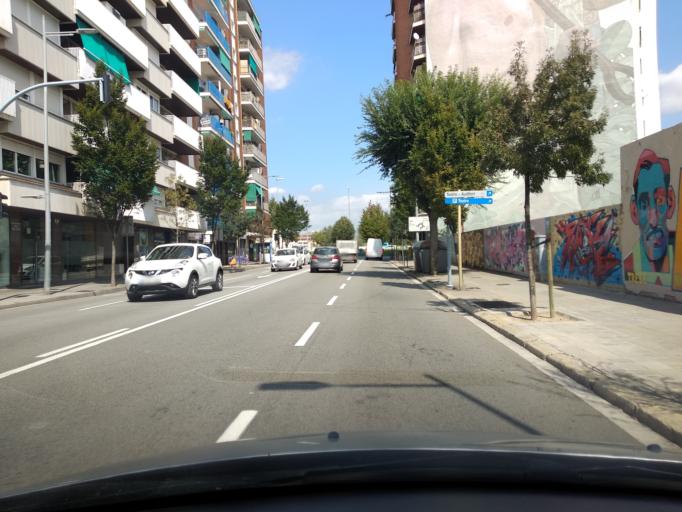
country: ES
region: Catalonia
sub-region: Provincia de Barcelona
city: Granollers
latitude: 41.6100
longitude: 2.2835
